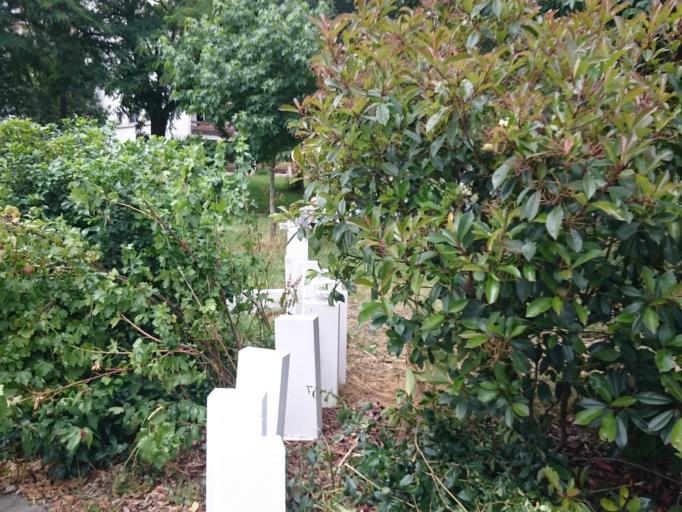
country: FR
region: Brittany
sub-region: Departement d'Ille-et-Vilaine
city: Rennes
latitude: 48.1103
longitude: -1.6908
